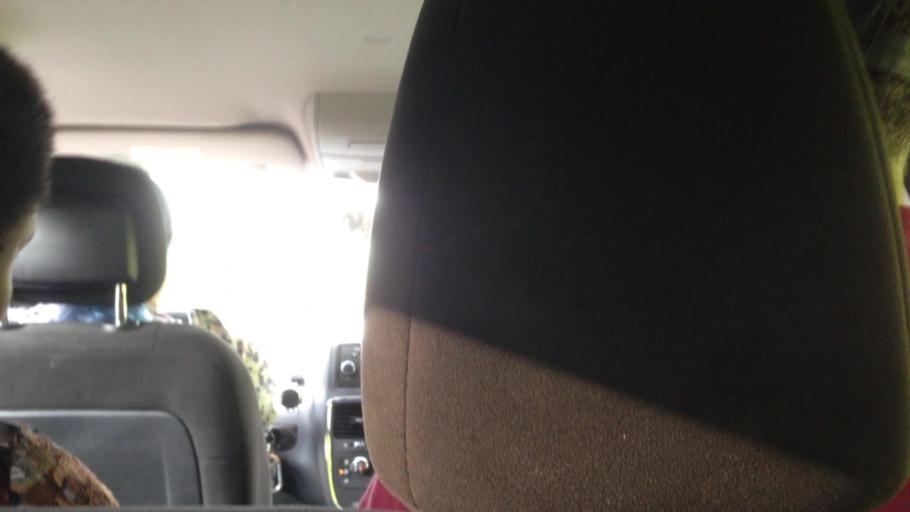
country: US
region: New York
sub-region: Dutchess County
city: Red Hook
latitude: 41.9992
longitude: -73.9093
